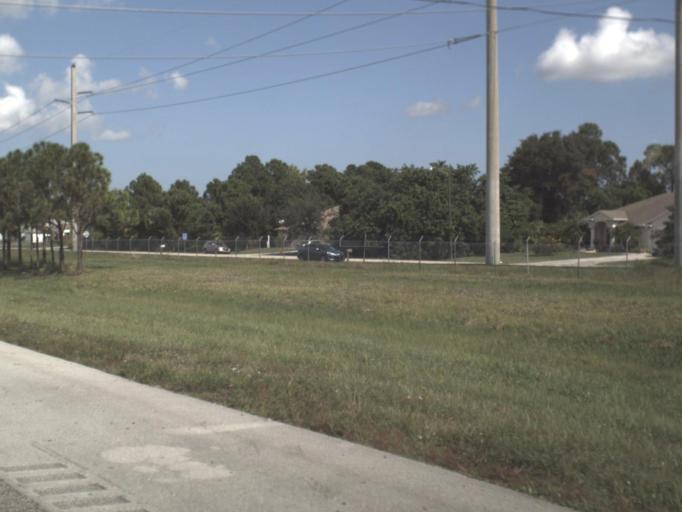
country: US
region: Florida
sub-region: Saint Lucie County
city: River Park
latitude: 27.3188
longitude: -80.3743
